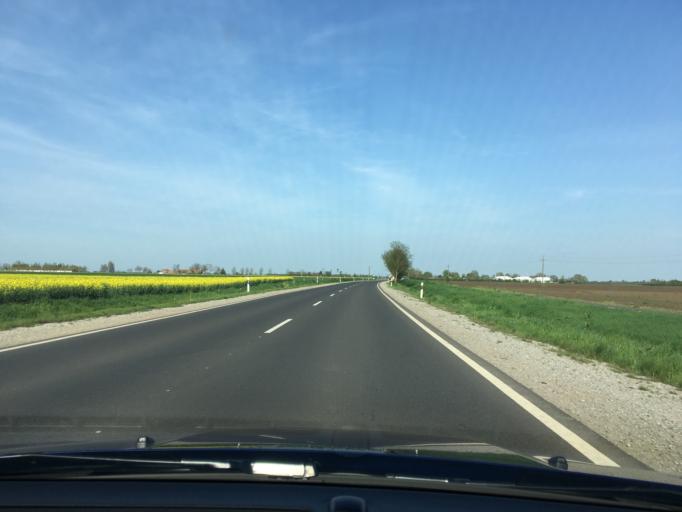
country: HU
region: Bekes
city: Csorvas
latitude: 46.6515
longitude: 20.9106
